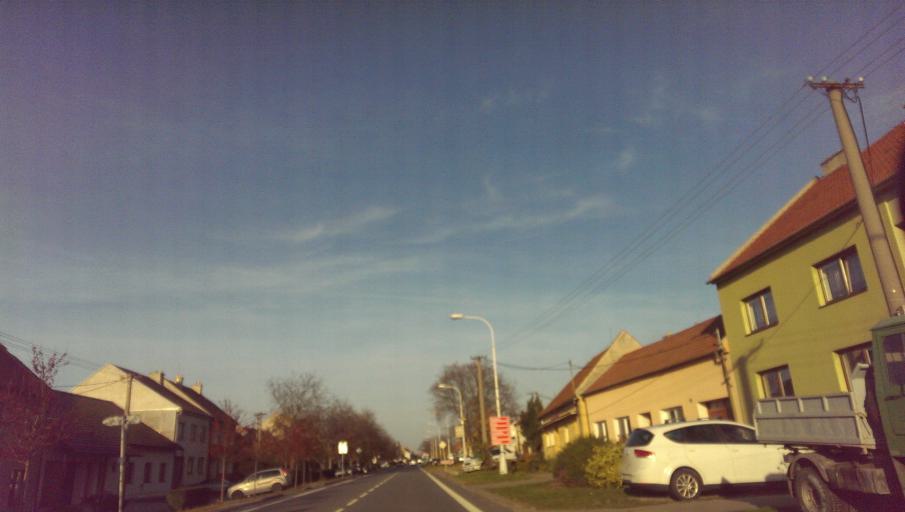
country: CZ
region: Zlin
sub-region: Okres Zlin
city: Ostrozska Nova Ves
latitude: 49.0023
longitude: 17.4323
